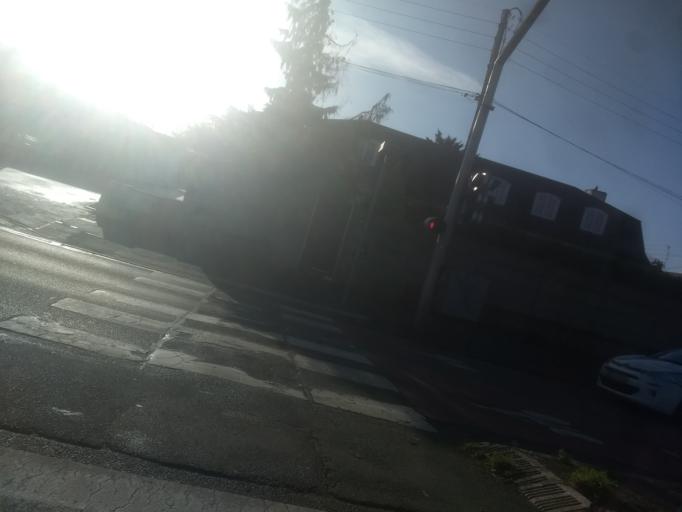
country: FR
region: Nord-Pas-de-Calais
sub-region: Departement du Pas-de-Calais
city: Anzin-Saint-Aubin
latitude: 50.2982
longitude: 2.7490
